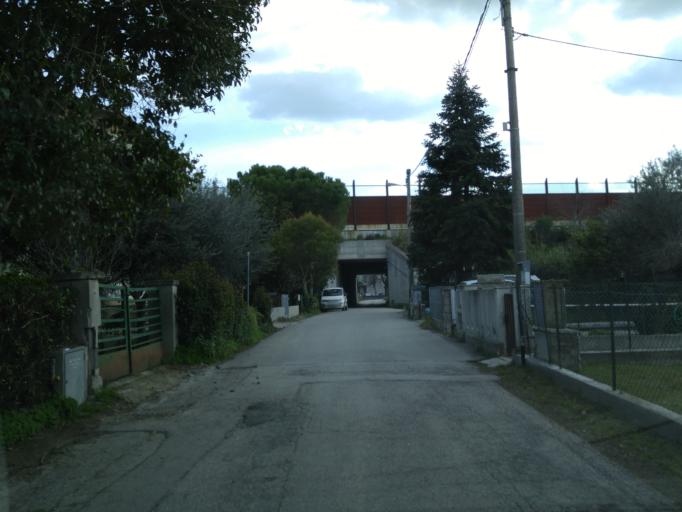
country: IT
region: The Marches
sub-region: Provincia di Pesaro e Urbino
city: Rosciano
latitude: 43.8151
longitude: 13.0196
